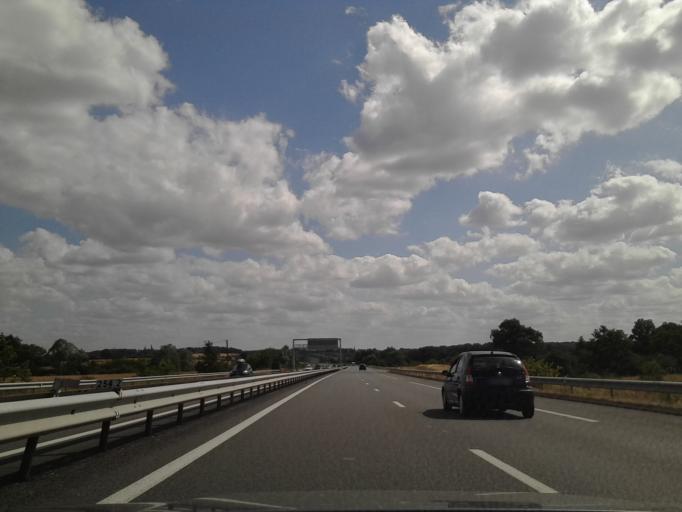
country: FR
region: Centre
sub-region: Departement du Cher
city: Orval
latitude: 46.6935
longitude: 2.4614
